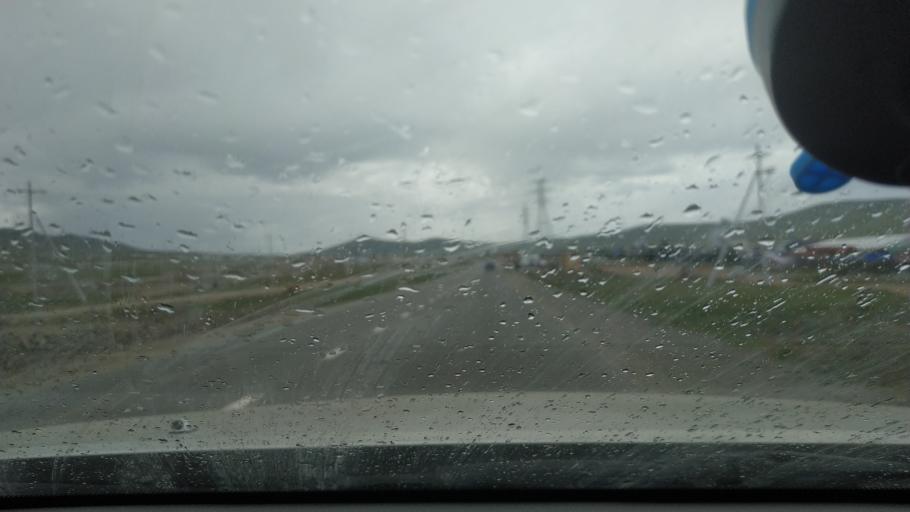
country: MN
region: Ulaanbaatar
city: Ulaanbaatar
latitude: 47.8204
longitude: 106.7606
